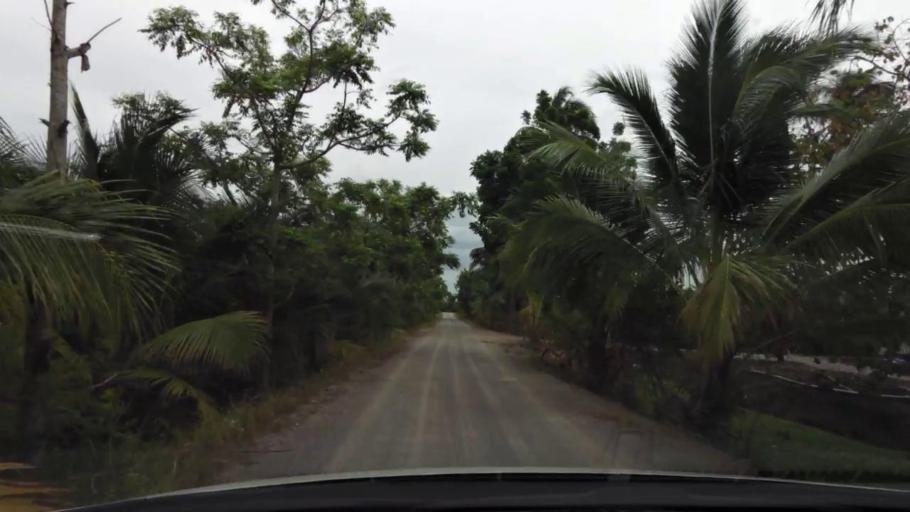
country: TH
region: Ratchaburi
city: Damnoen Saduak
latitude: 13.5623
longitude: 100.0162
